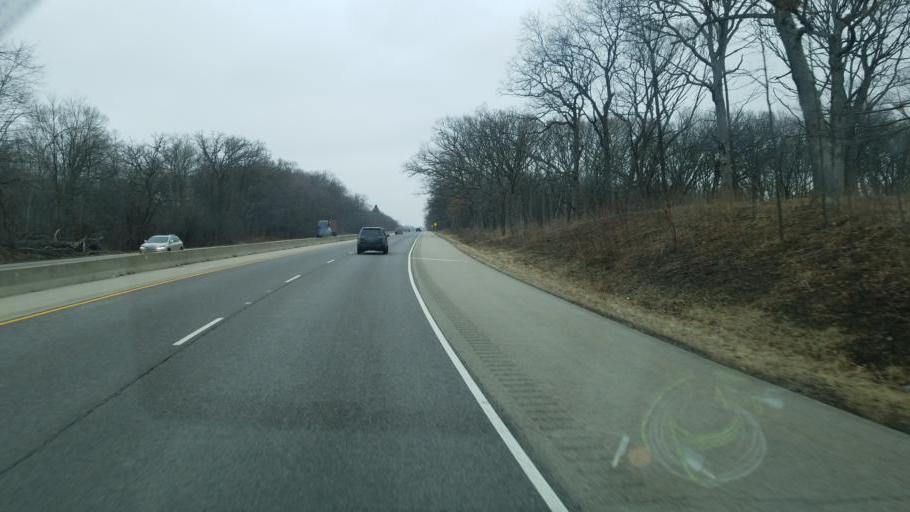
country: US
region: Illinois
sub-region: Lake County
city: Wadsworth
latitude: 42.4510
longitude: -87.9454
